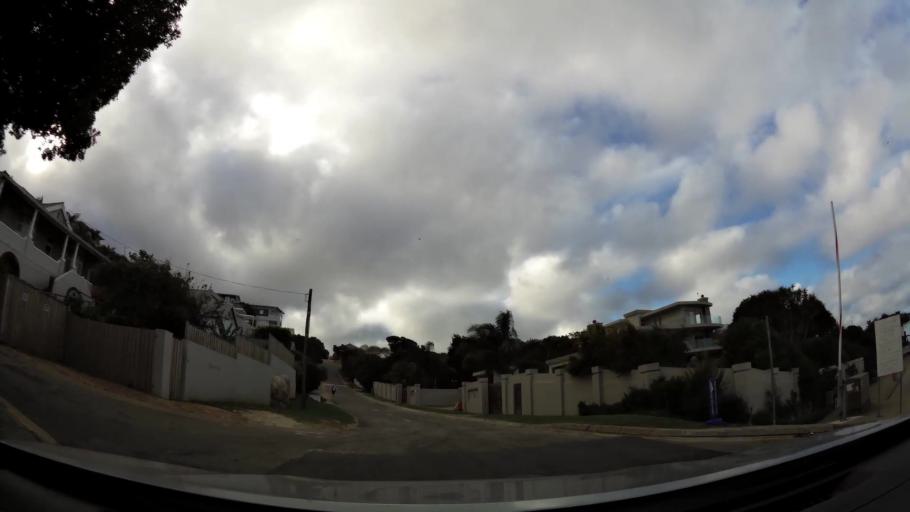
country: ZA
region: Western Cape
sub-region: Eden District Municipality
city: Plettenberg Bay
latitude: -34.0596
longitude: 23.3769
